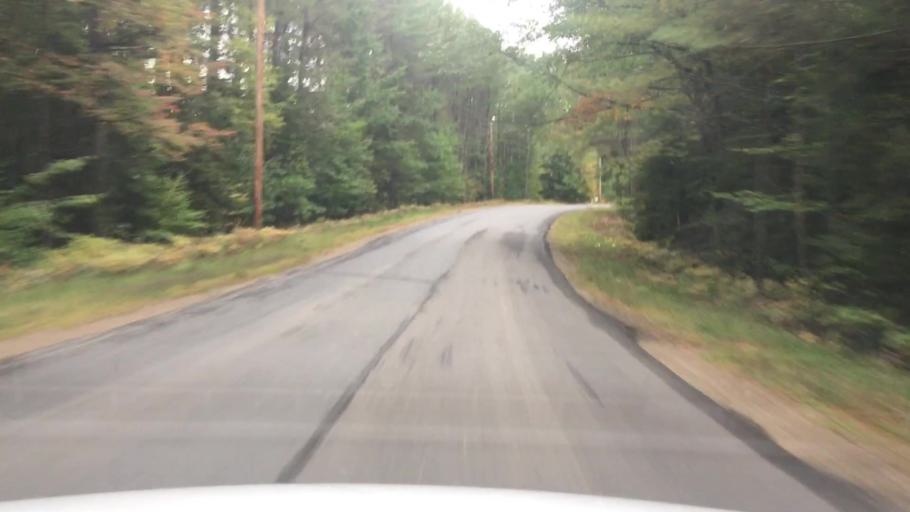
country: US
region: Maine
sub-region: Oxford County
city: Bethel
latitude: 44.4438
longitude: -70.7951
